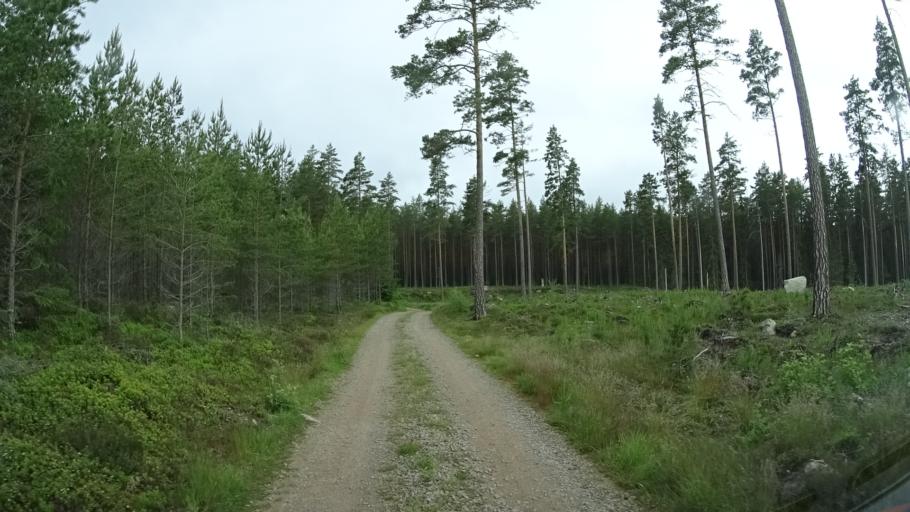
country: SE
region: Kalmar
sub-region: Vimmerby Kommun
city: Sodra Vi
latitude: 57.7161
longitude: 15.7763
